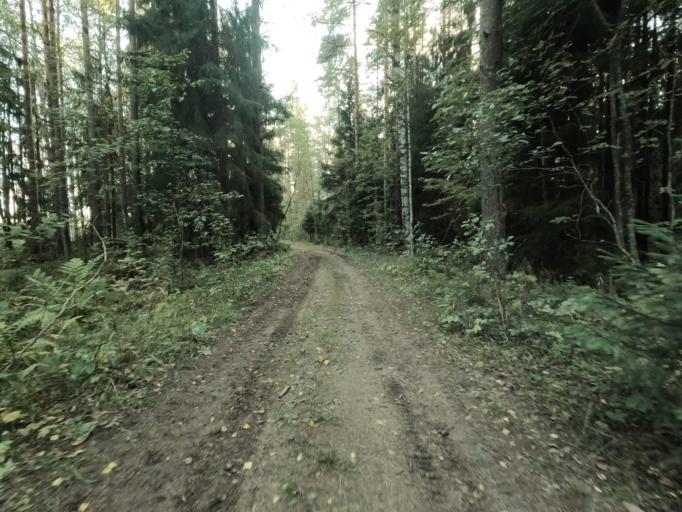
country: RU
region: Leningrad
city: Otradnoye
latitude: 59.8430
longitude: 30.7817
